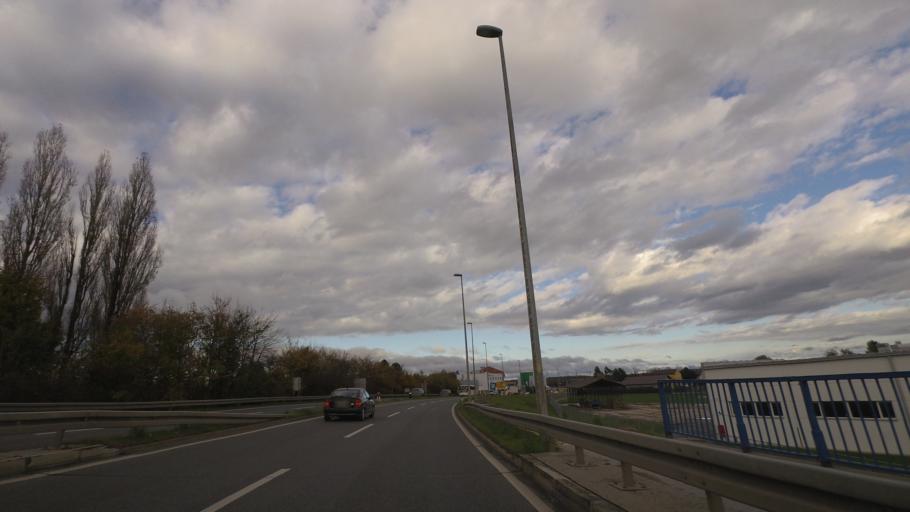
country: HR
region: Karlovacka
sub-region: Grad Karlovac
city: Karlovac
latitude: 45.5109
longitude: 15.5434
